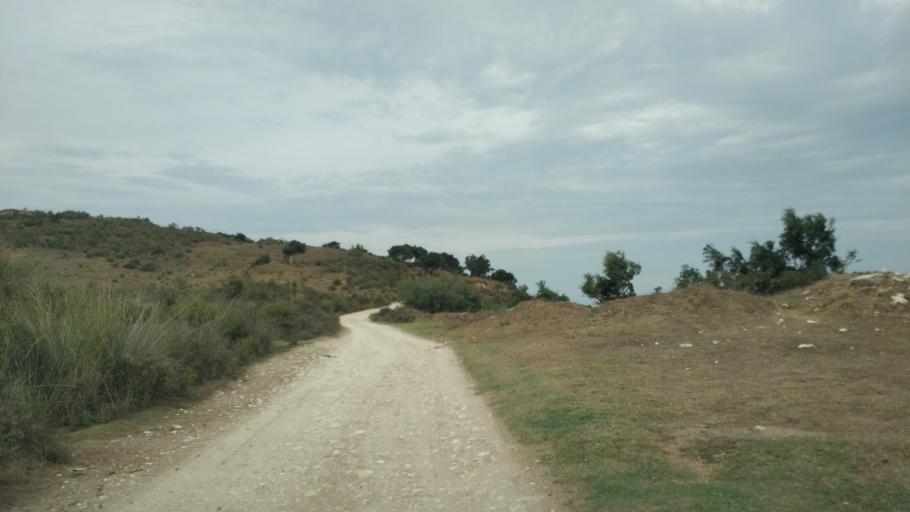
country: AL
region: Vlore
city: Vlore
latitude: 40.5152
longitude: 19.3951
